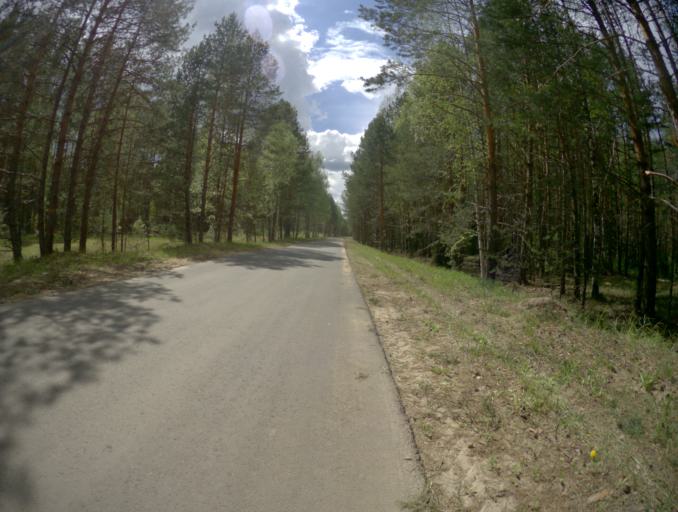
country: RU
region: Vladimir
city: Velikodvorskiy
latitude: 55.2498
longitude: 40.7656
